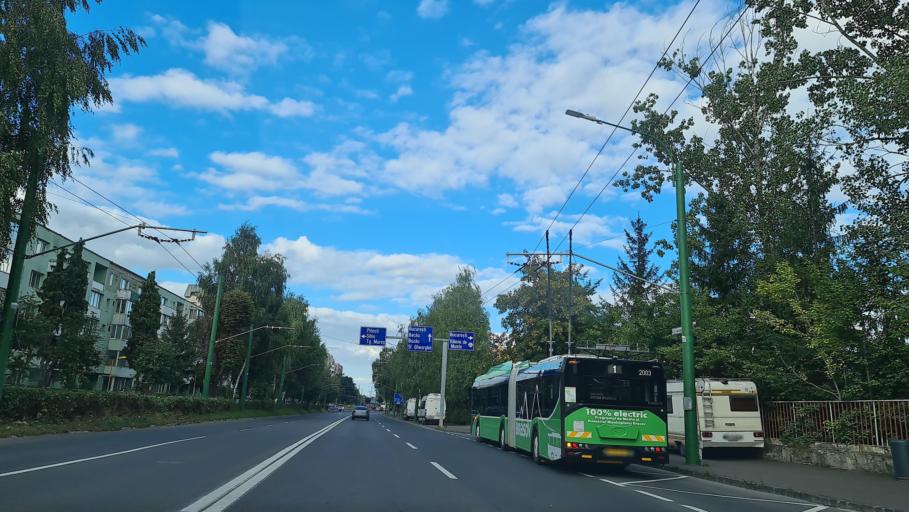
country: RO
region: Brasov
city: Brasov
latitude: 45.6564
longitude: 25.6186
